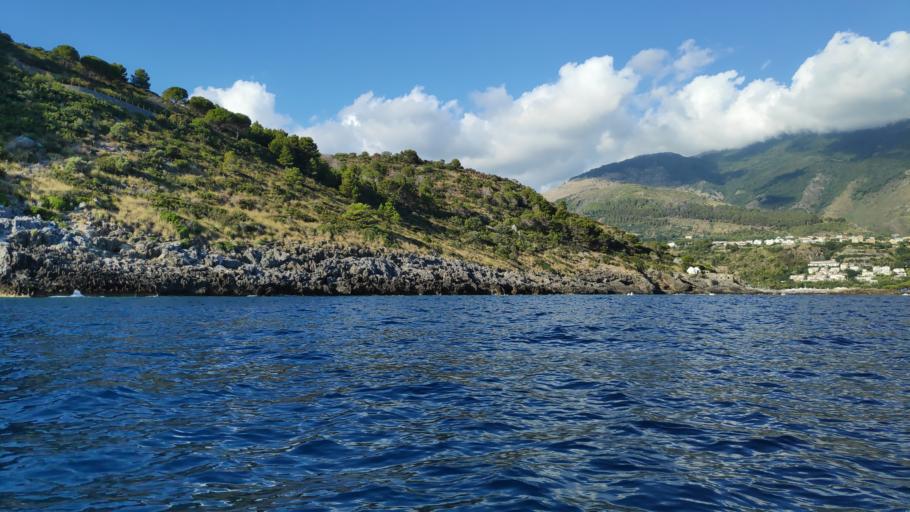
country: IT
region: Calabria
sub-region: Provincia di Cosenza
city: Praia a Mare
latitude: 39.8711
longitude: 15.7745
